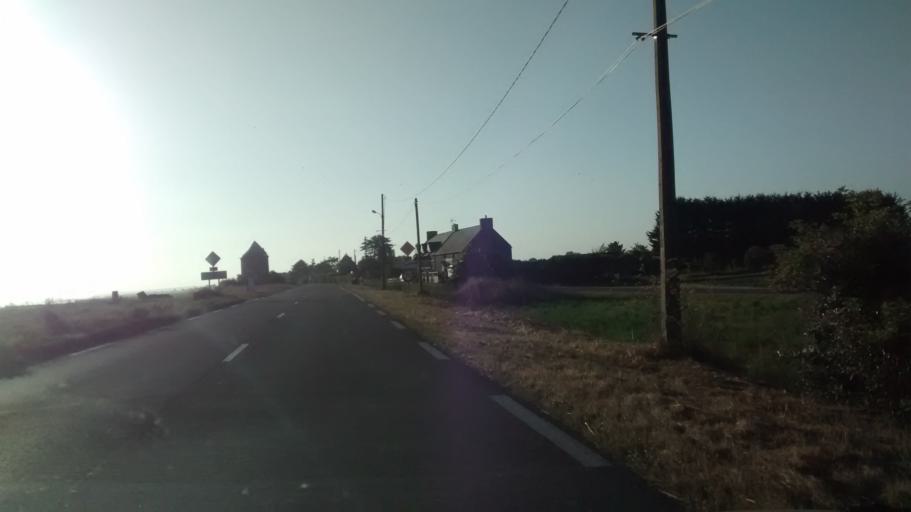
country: FR
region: Brittany
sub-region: Departement d'Ille-et-Vilaine
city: La Fresnais
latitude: 48.6109
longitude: -1.8275
